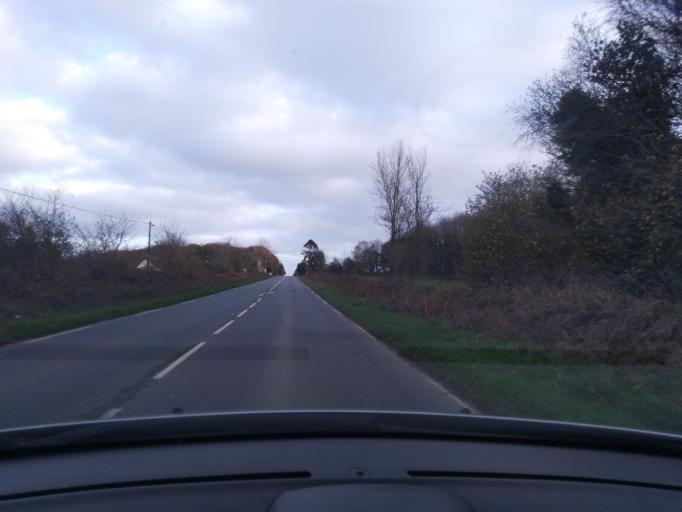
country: FR
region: Brittany
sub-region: Departement du Finistere
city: Plouigneau
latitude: 48.5734
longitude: -3.7429
